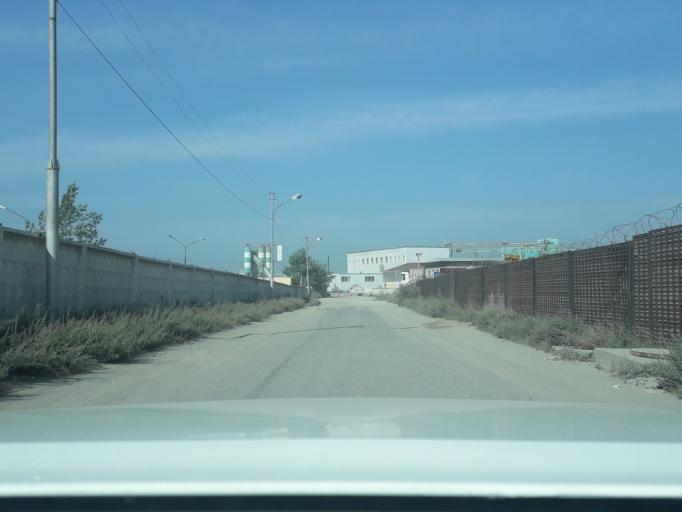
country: MN
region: Ulaanbaatar
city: Ulaanbaatar
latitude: 47.9070
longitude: 106.8850
